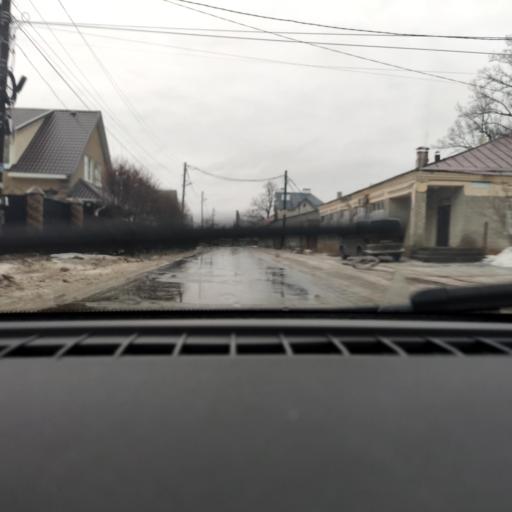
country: RU
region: Voronezj
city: Somovo
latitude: 51.7372
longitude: 39.3559
